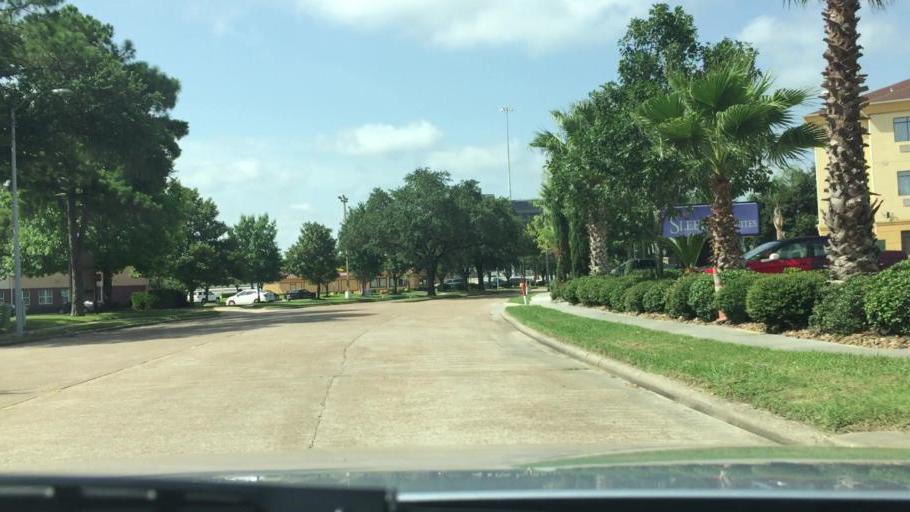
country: US
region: Texas
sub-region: Harris County
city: Spring Valley
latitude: 29.8454
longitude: -95.4949
